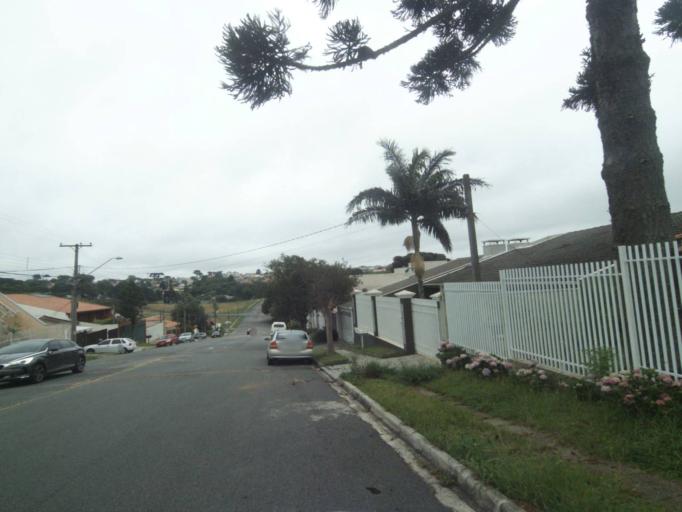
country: BR
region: Parana
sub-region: Curitiba
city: Curitiba
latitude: -25.4294
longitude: -49.3464
